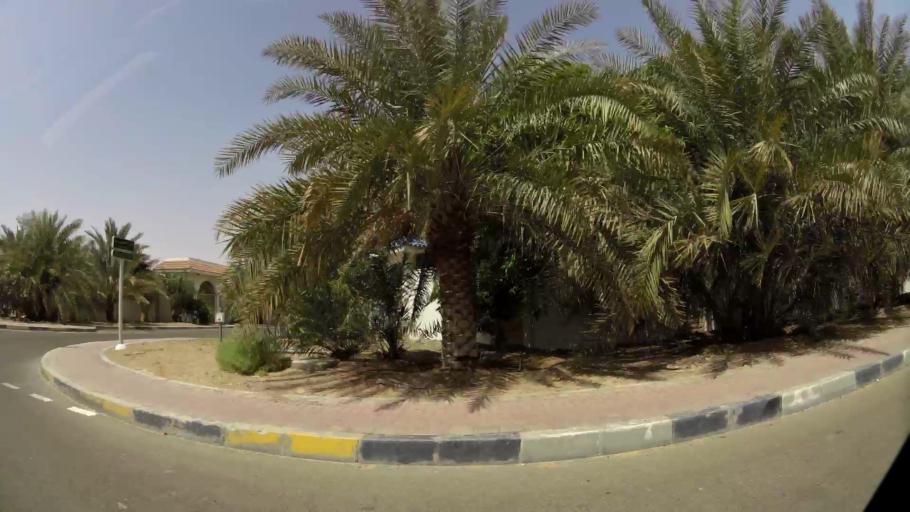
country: AE
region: Abu Dhabi
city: Al Ain
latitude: 24.1866
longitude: 55.7304
